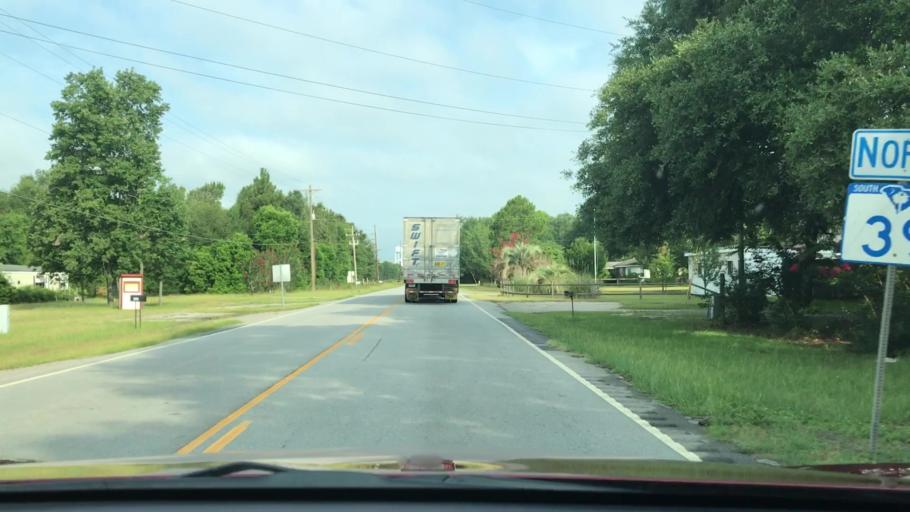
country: US
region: South Carolina
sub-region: Barnwell County
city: Williston
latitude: 33.6352
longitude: -81.3198
